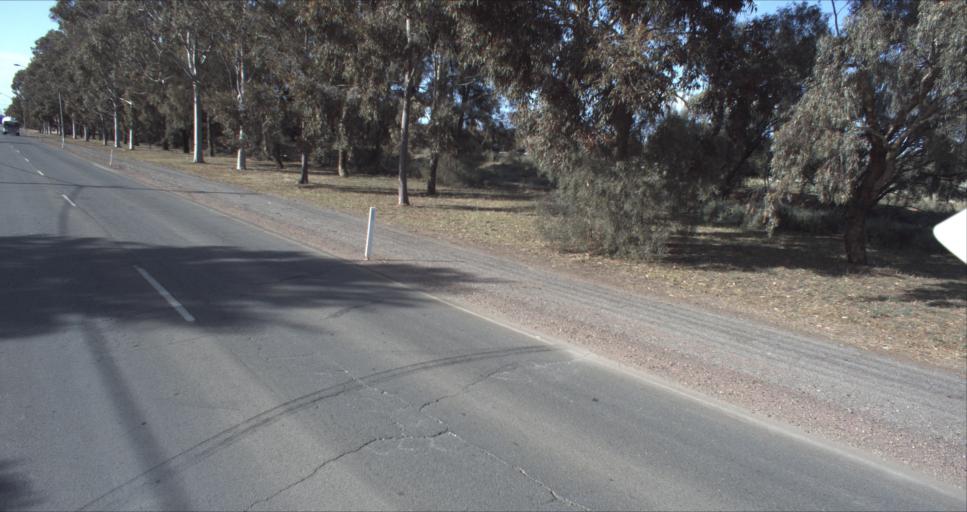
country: AU
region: New South Wales
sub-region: Leeton
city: Leeton
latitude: -34.5568
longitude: 146.3894
